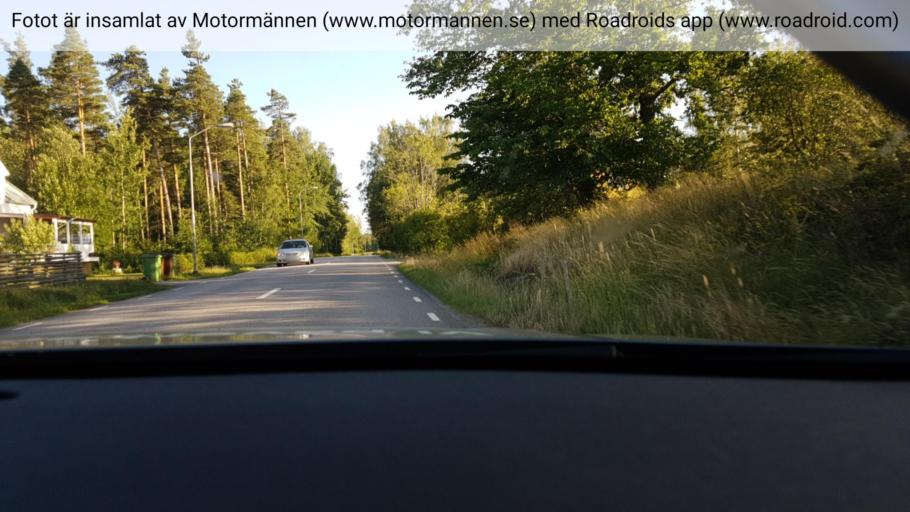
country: SE
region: Vaestra Goetaland
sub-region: Skovde Kommun
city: Stopen
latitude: 58.5619
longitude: 14.0078
